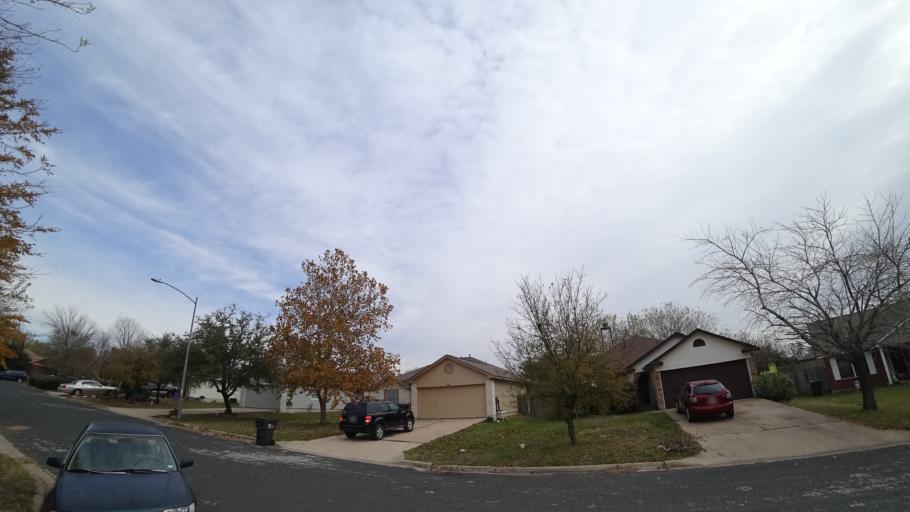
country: US
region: Texas
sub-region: Travis County
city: Garfield
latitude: 30.1562
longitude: -97.6478
